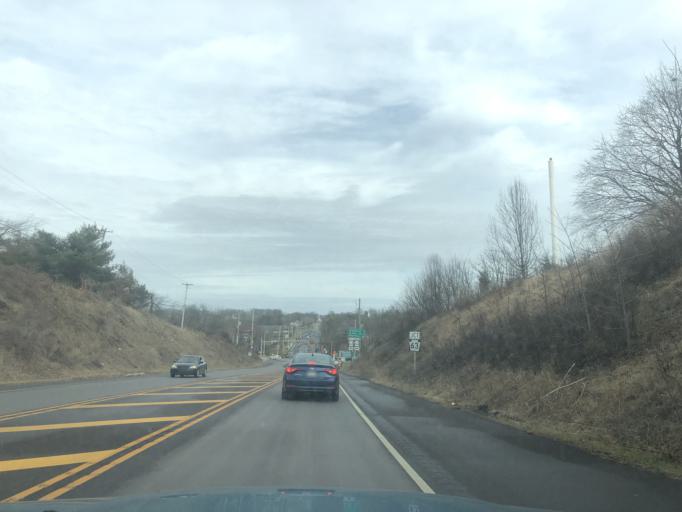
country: US
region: Pennsylvania
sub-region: Montgomery County
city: Harleysville
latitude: 40.2811
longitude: -75.3936
